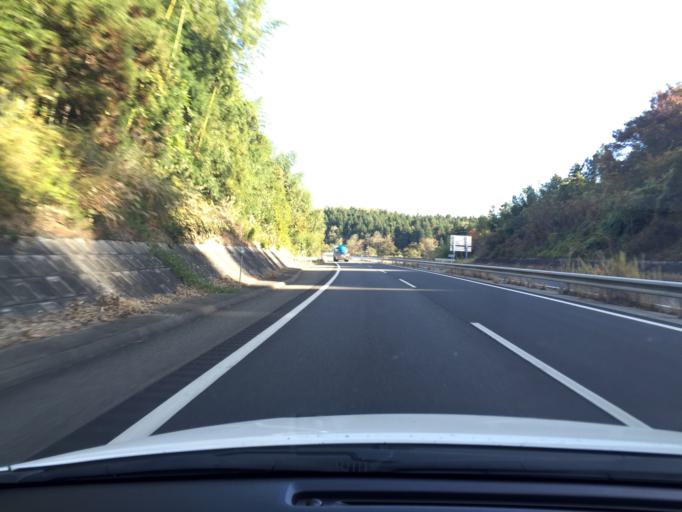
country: JP
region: Fukushima
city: Miharu
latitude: 37.4397
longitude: 140.4451
